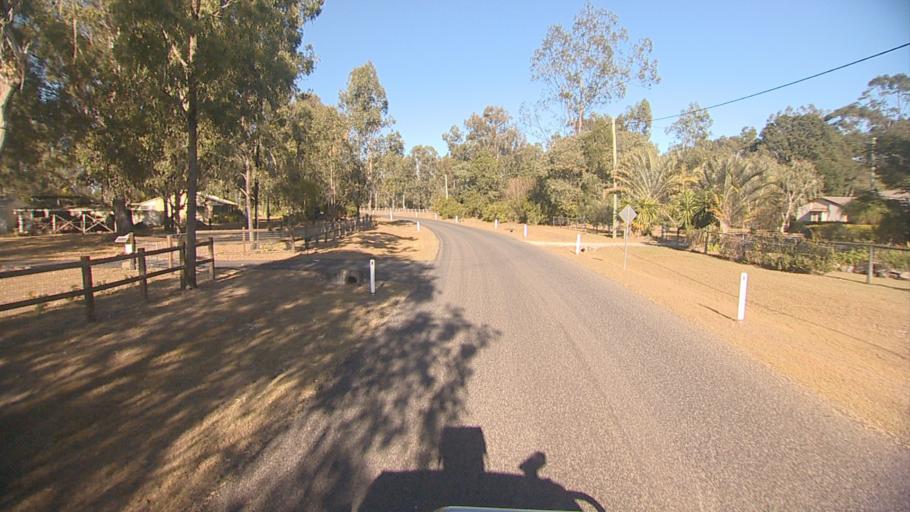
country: AU
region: Queensland
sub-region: Logan
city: North Maclean
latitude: -27.8271
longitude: 152.9907
